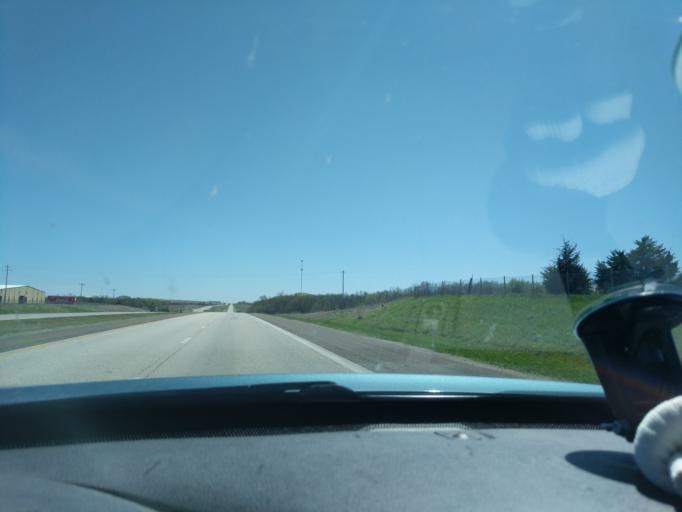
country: US
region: Kansas
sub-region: Republic County
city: Belleville
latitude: 39.7043
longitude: -97.6605
